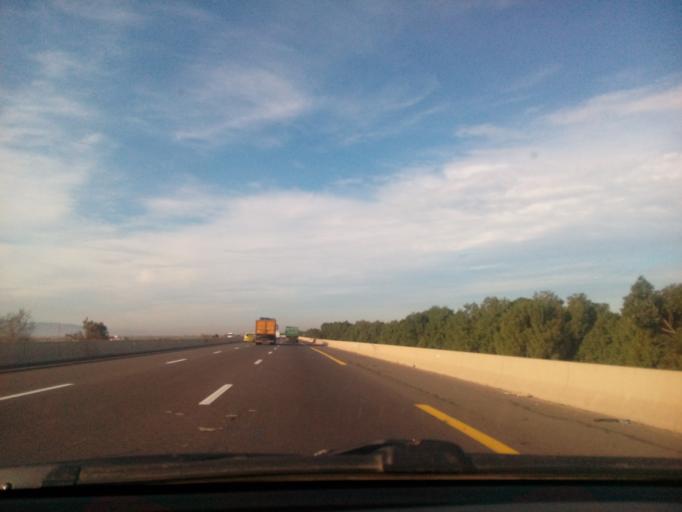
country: DZ
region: Mascara
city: Sig
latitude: 35.5870
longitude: -0.1205
